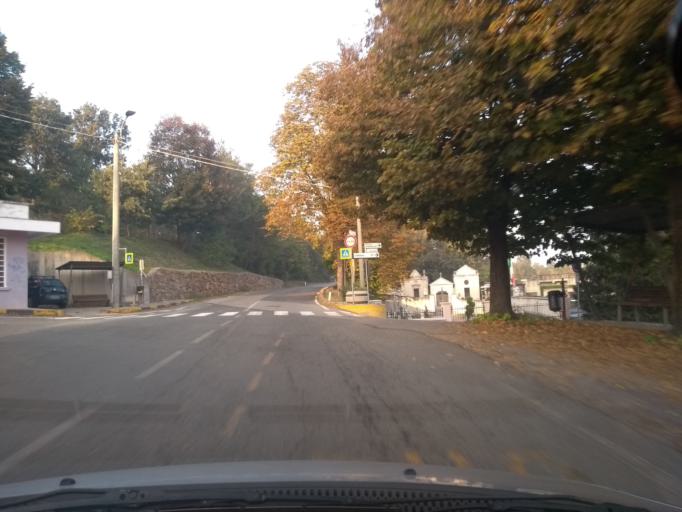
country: IT
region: Piedmont
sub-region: Provincia di Torino
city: Givoletto
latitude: 45.1607
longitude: 7.4996
